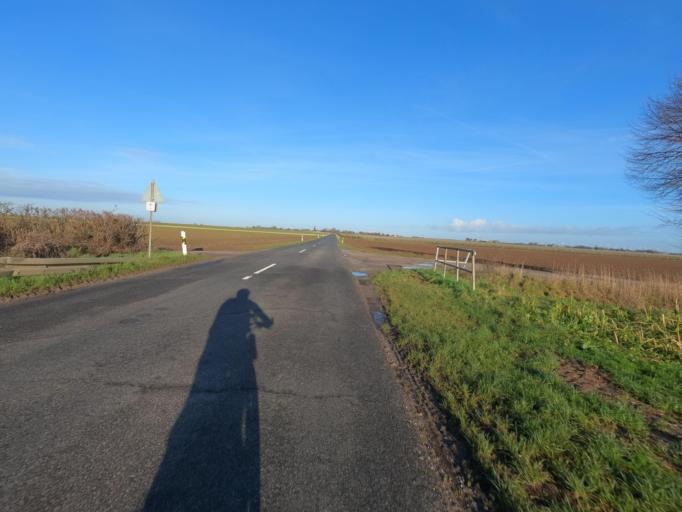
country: DE
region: North Rhine-Westphalia
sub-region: Regierungsbezirk Koln
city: Titz
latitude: 50.9656
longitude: 6.4113
